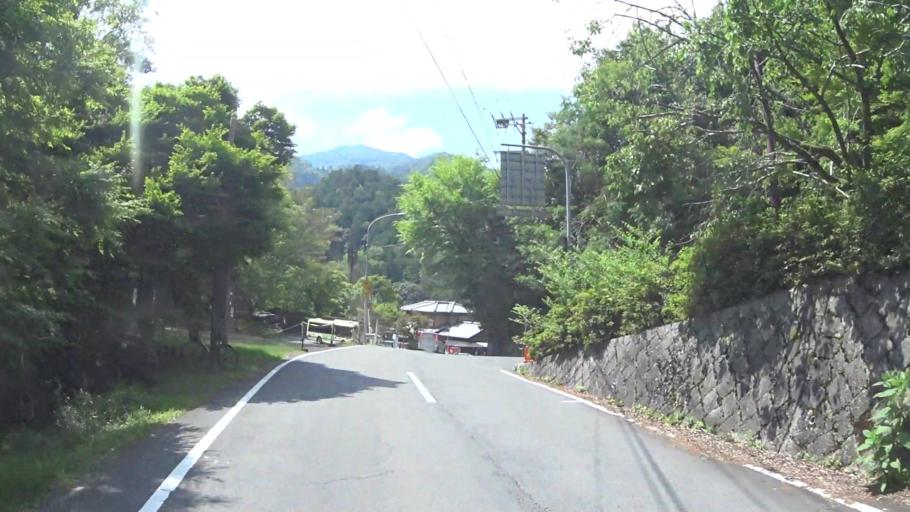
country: JP
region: Kyoto
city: Kameoka
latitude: 35.0357
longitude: 135.6589
